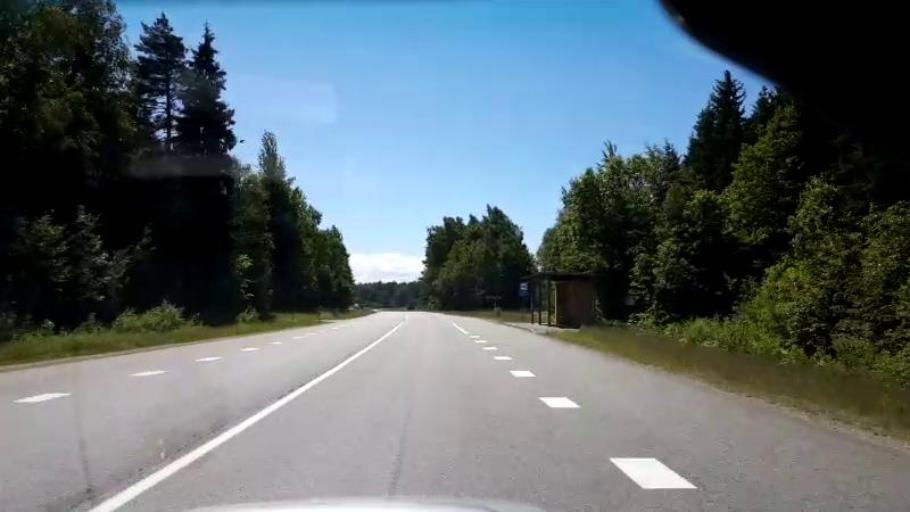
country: LV
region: Saulkrastu
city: Saulkrasti
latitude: 57.4179
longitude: 24.4288
